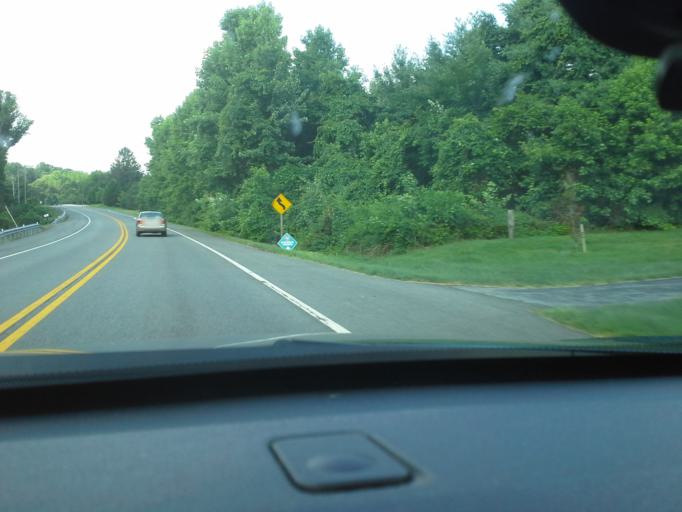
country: US
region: Maryland
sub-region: Calvert County
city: Huntingtown
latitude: 38.6125
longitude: -76.5638
